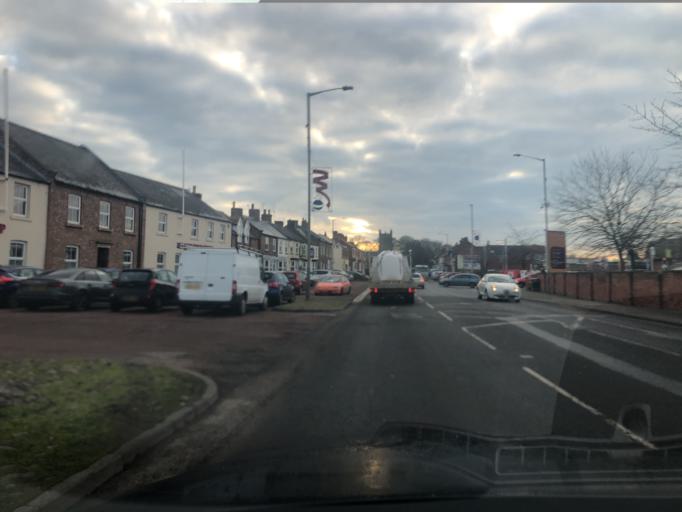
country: GB
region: England
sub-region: North Yorkshire
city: Northallerton
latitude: 54.3451
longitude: -1.4388
